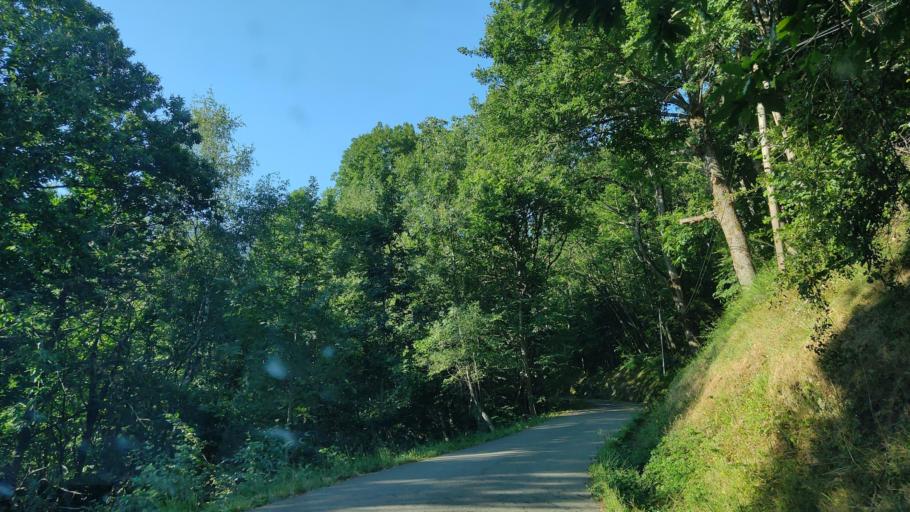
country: FR
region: Rhone-Alpes
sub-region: Departement de la Savoie
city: Saint-Etienne-de-Cuines
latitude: 45.3408
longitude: 6.2802
